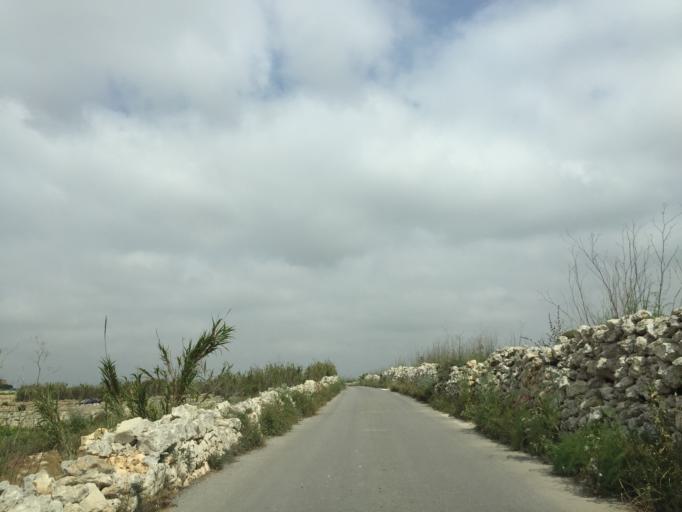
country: MT
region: L-Imtarfa
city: Imtarfa
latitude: 35.9025
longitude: 14.3822
